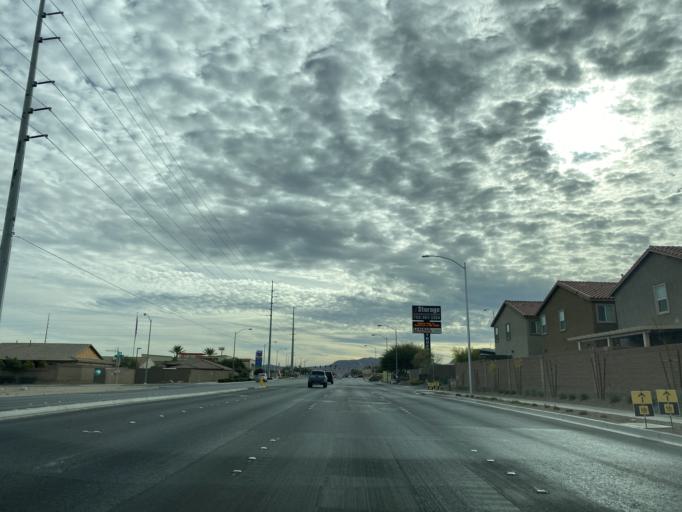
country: US
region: Nevada
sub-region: Clark County
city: Enterprise
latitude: 36.0235
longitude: -115.2790
